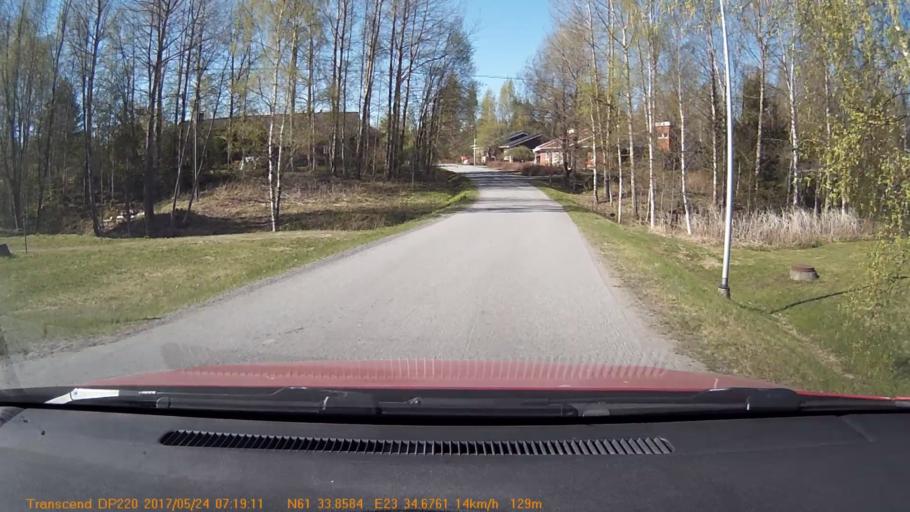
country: FI
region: Pirkanmaa
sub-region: Tampere
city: Yloejaervi
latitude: 61.5642
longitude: 23.5779
